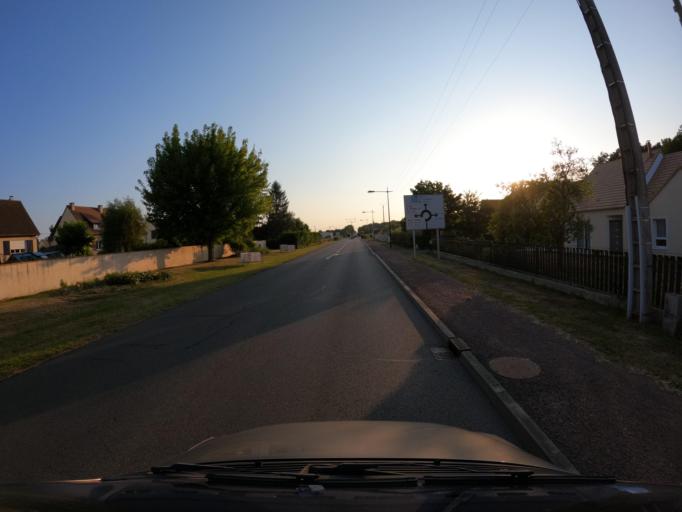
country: FR
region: Pays de la Loire
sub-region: Departement de la Sarthe
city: Parce-sur-Sarthe
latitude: 47.8431
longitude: -0.2072
